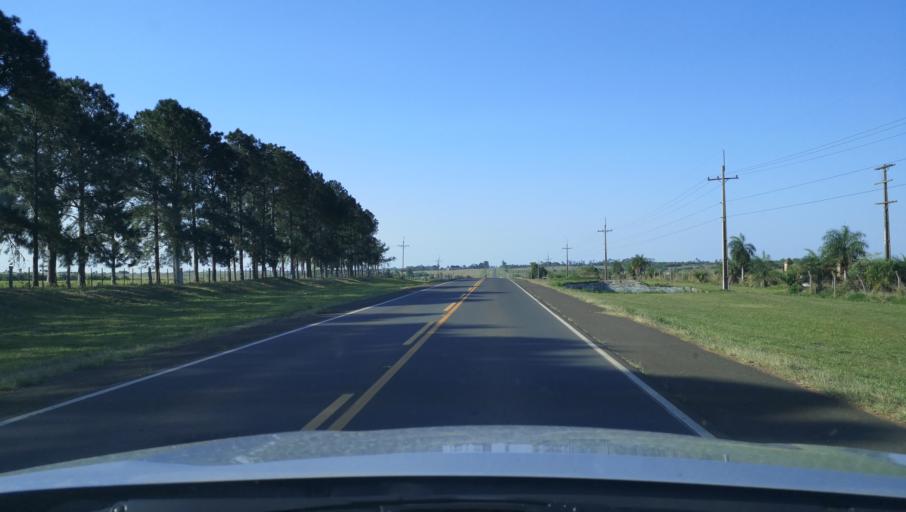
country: PY
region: Misiones
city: Santa Maria
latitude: -26.8405
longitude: -57.0360
